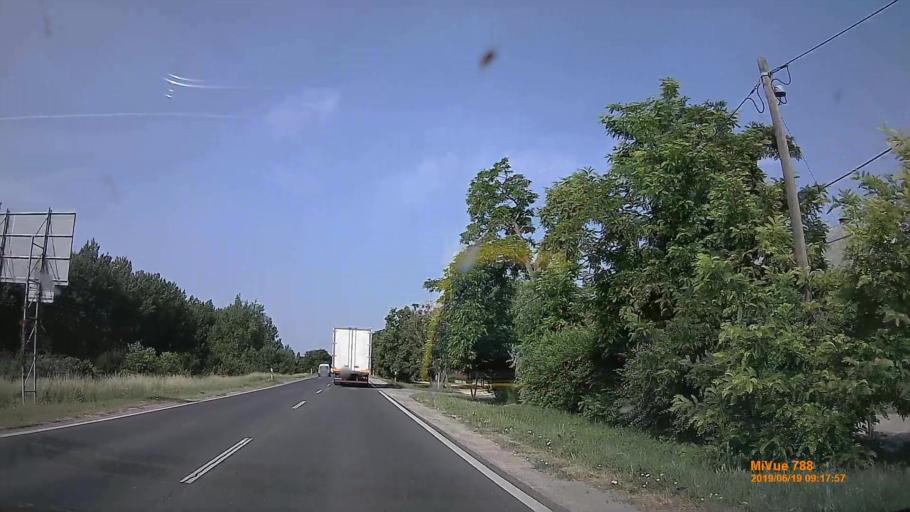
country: HU
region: Pest
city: Diosd
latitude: 47.3830
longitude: 18.9520
